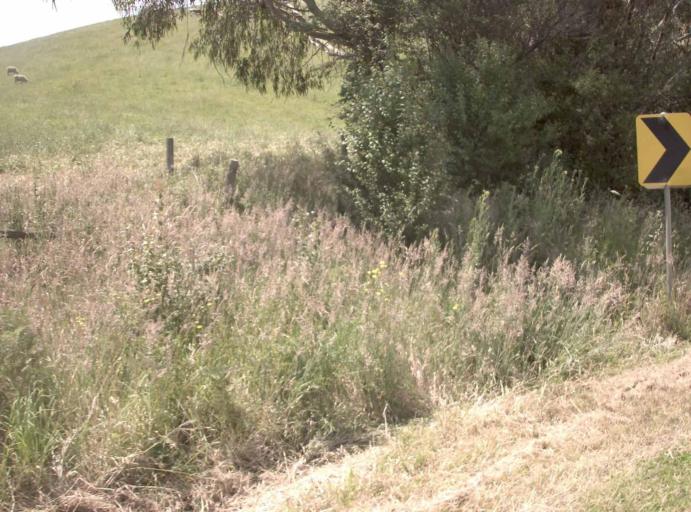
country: AU
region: Victoria
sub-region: Baw Baw
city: Warragul
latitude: -38.4851
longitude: 145.9938
